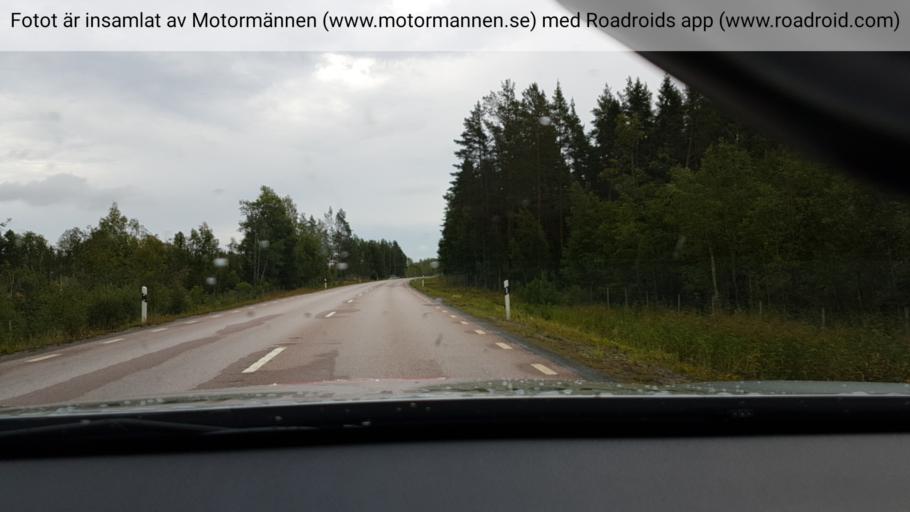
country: SE
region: Uppsala
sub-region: Osthammars Kommun
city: Osterbybruk
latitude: 60.4262
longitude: 17.8360
